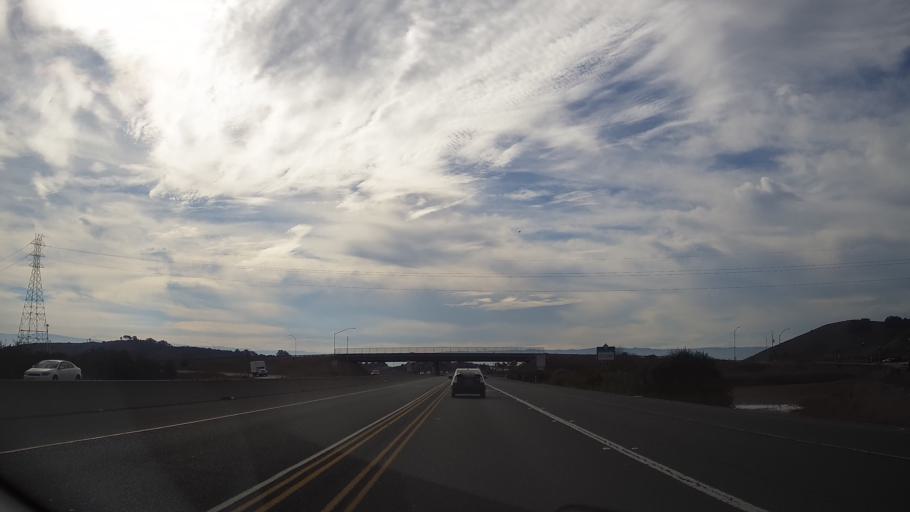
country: US
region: California
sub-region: Alameda County
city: Newark
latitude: 37.5422
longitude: -122.0652
